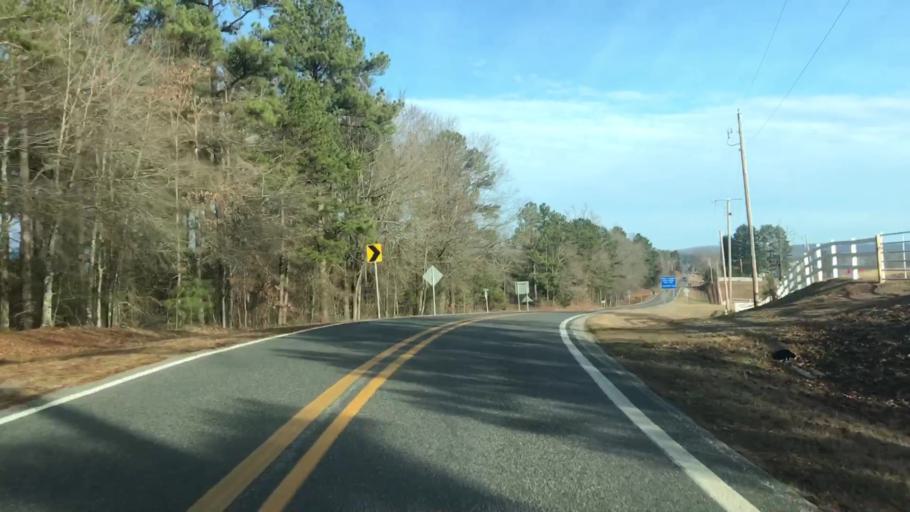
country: US
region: Arkansas
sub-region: Garland County
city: Rockwell
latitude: 34.4948
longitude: -93.2766
